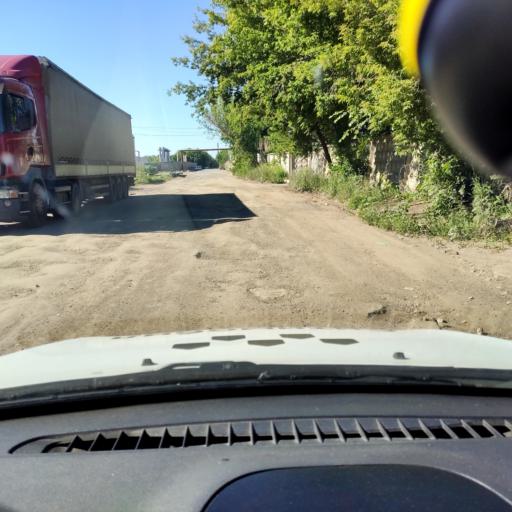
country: RU
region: Samara
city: Tol'yatti
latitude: 53.5878
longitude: 49.2579
